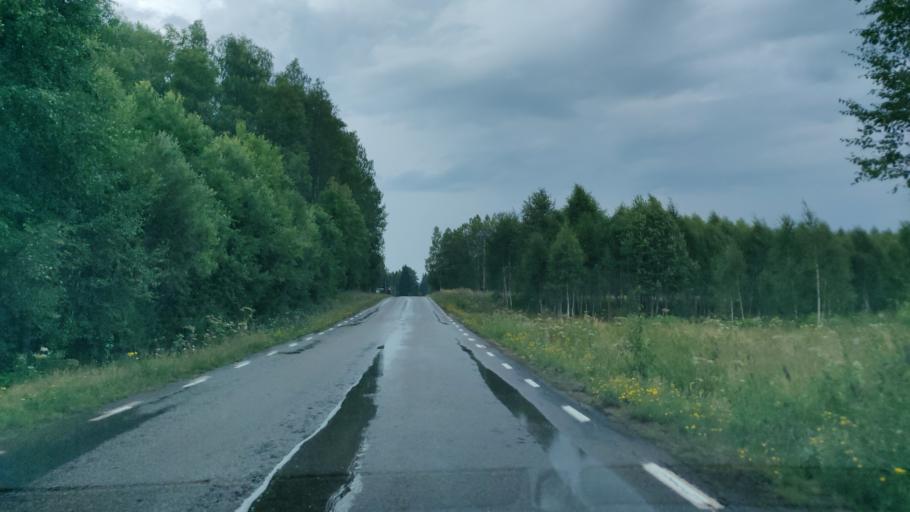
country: SE
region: Vaermland
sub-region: Munkfors Kommun
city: Munkfors
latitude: 59.8728
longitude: 13.5289
